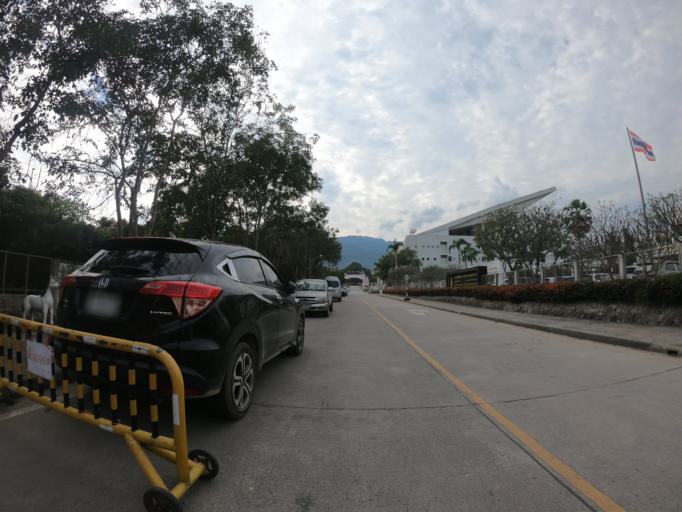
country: TH
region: Chiang Mai
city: Chiang Mai
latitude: 18.8501
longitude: 98.9631
